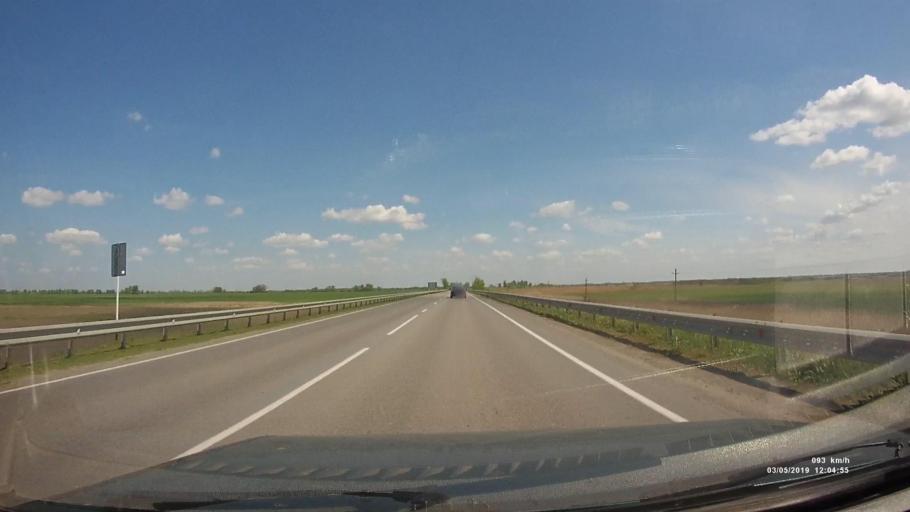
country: RU
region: Rostov
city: Bagayevskaya
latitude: 47.2814
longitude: 40.4189
